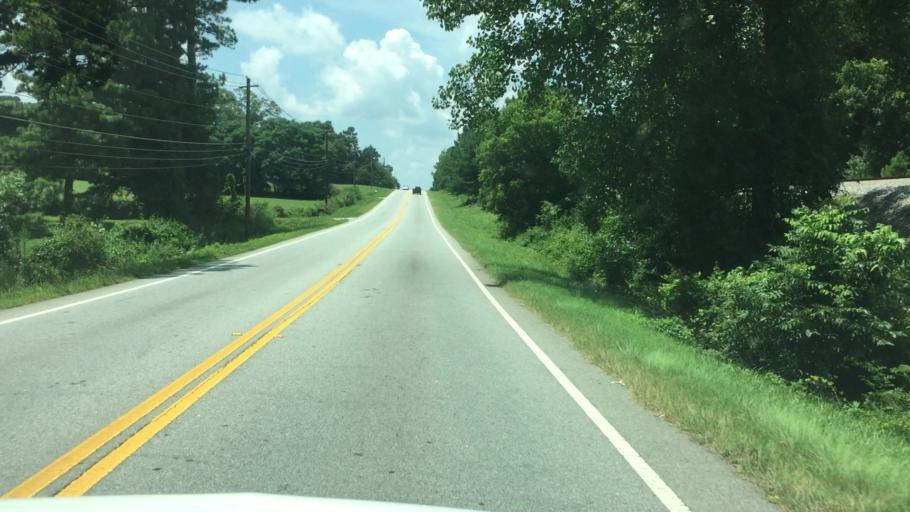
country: US
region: Georgia
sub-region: Barrow County
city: Auburn
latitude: 33.9979
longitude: -83.7922
